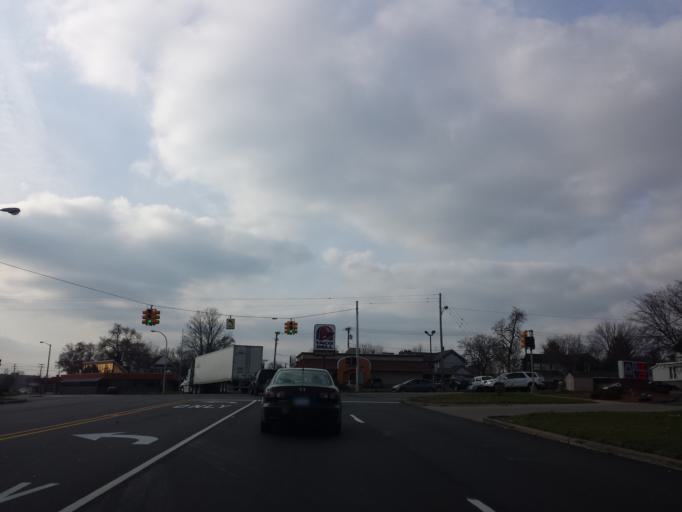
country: US
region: Michigan
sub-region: Wayne County
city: Plymouth
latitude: 42.3767
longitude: -83.4600
